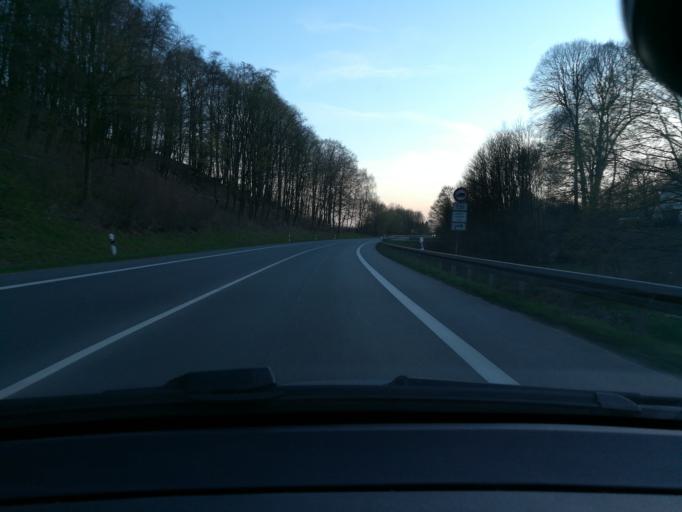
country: DE
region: North Rhine-Westphalia
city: Halle
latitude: 52.0727
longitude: 8.3660
